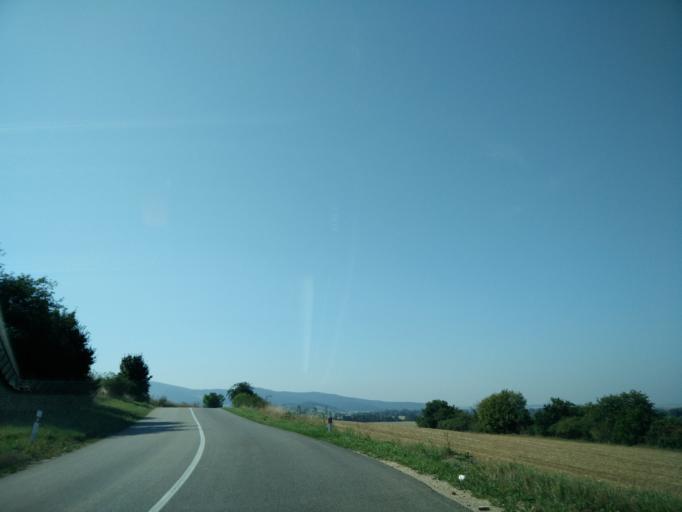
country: SK
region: Nitriansky
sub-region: Okres Nitra
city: Nitra
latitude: 48.4173
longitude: 18.1167
